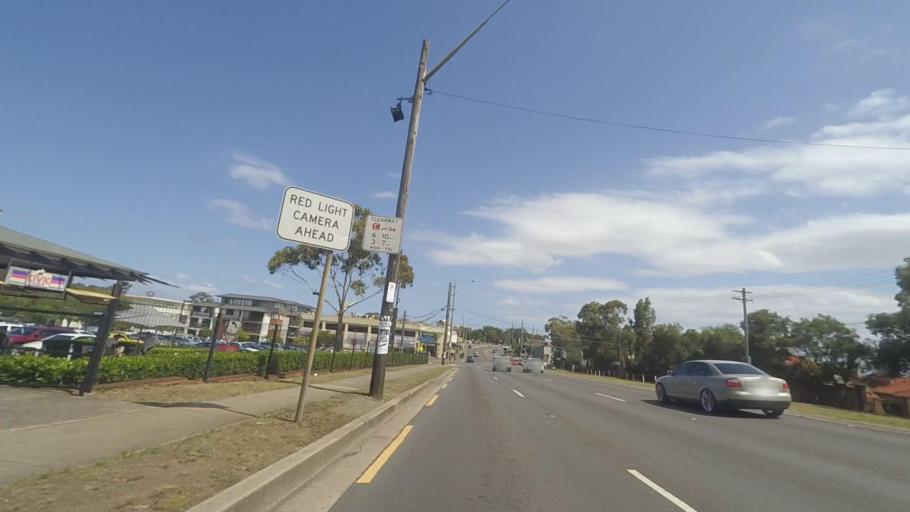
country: AU
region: New South Wales
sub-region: Parramatta
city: Carlingford
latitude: -33.7770
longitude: 151.0518
